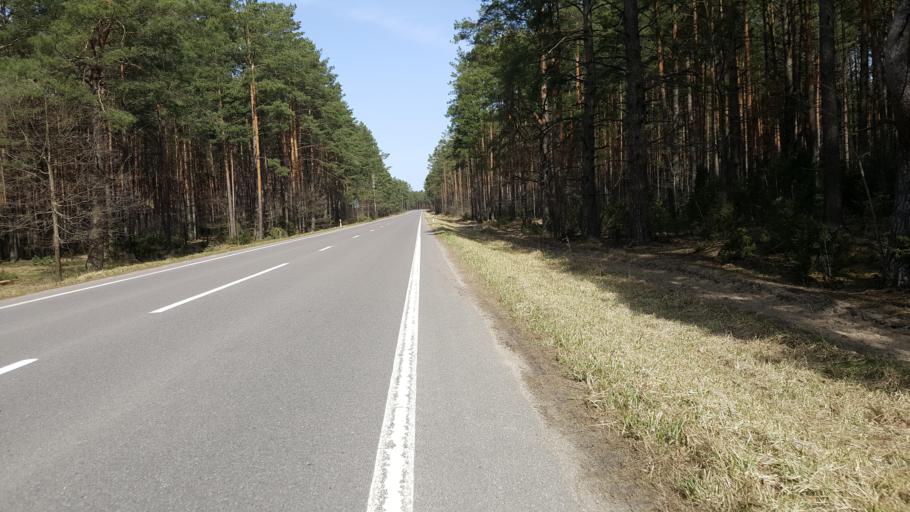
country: BY
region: Brest
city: Kamyanyuki
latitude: 52.5088
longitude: 23.6597
